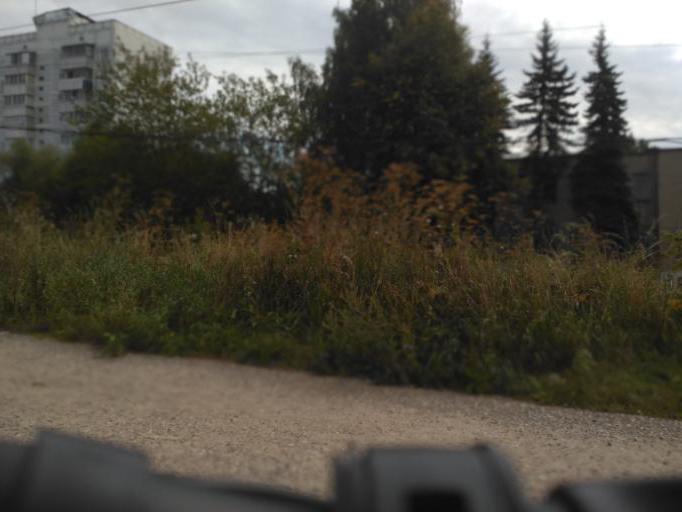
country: RU
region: Moskovskaya
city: Dubna
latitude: 56.7339
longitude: 37.1438
